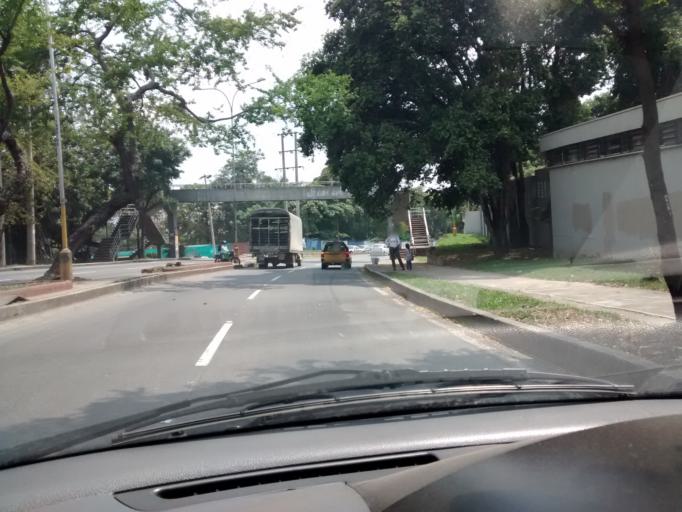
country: CO
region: Santander
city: Bucaramanga
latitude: 7.1003
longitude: -73.1131
